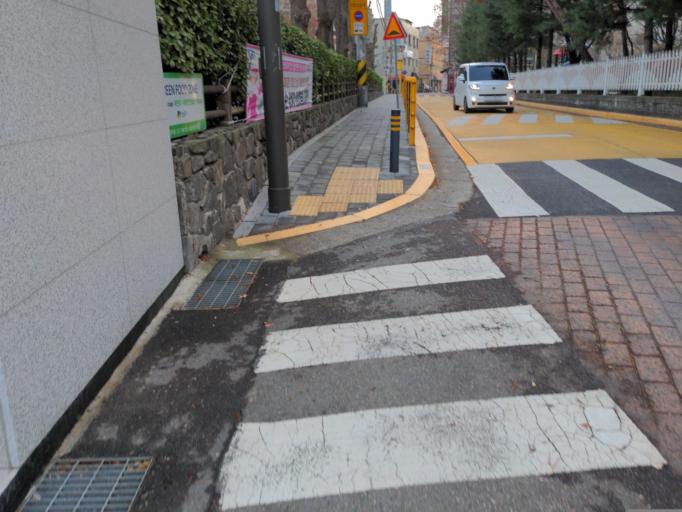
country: KR
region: Seoul
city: Seoul
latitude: 37.5394
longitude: 127.0578
